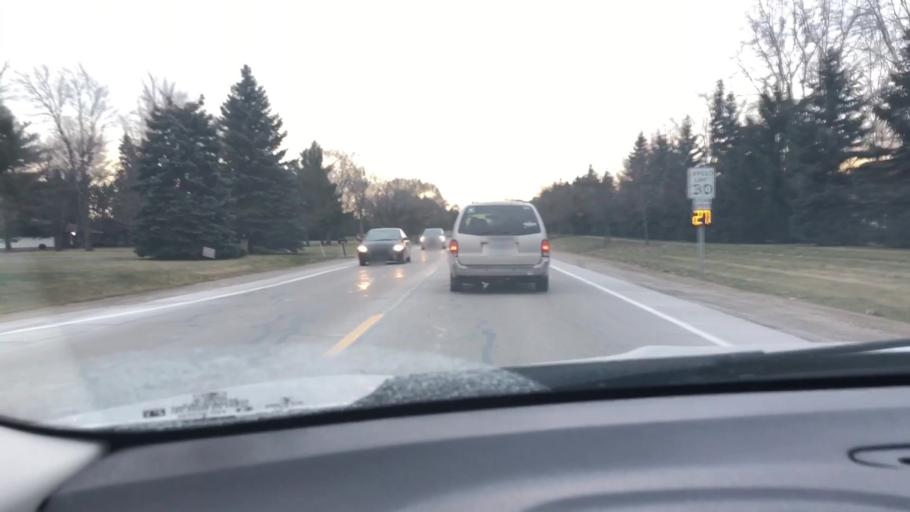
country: US
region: Michigan
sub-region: Wayne County
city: Northville
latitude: 42.4494
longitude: -83.4544
